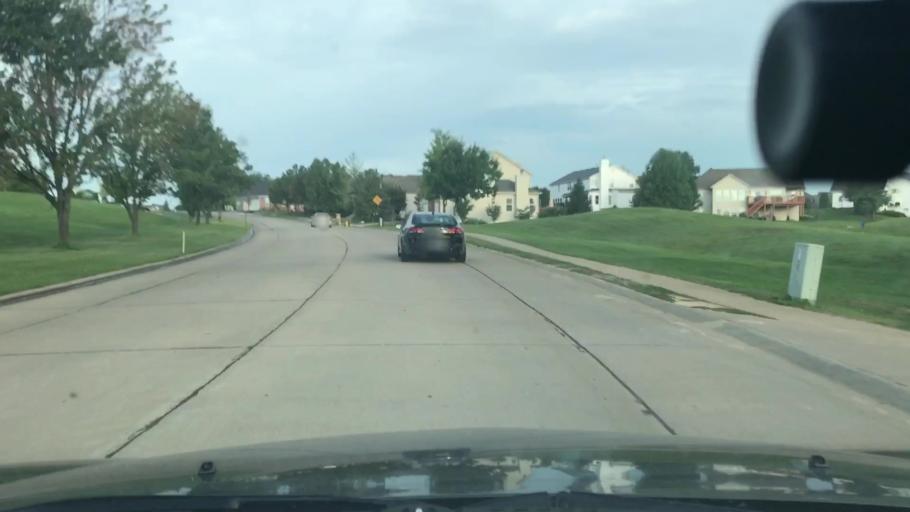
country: US
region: Missouri
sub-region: Saint Charles County
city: Wentzville
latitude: 38.8183
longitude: -90.8943
